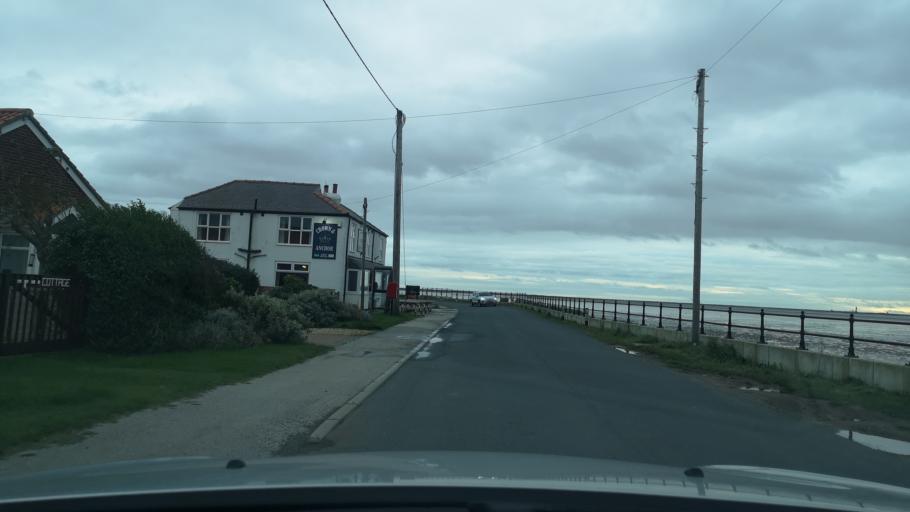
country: GB
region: England
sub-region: East Riding of Yorkshire
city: Easington
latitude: 53.6206
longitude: 0.1292
